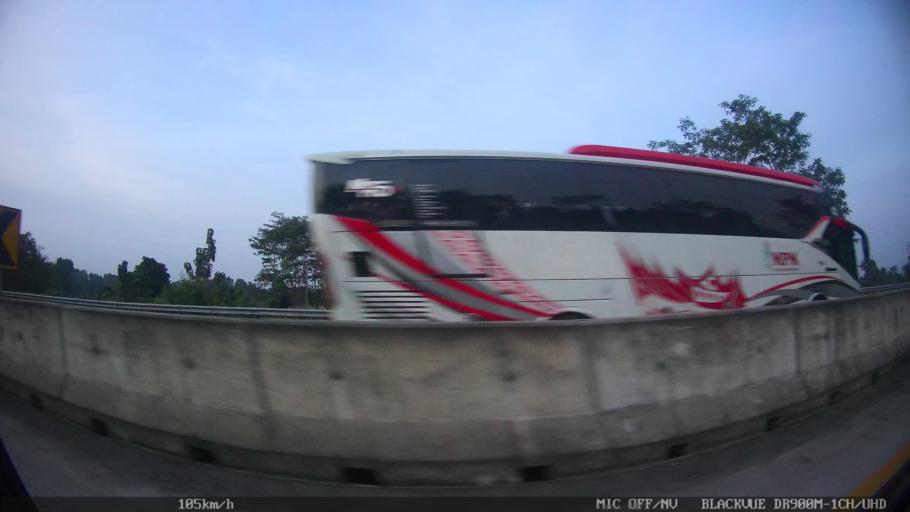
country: ID
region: Lampung
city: Penengahan
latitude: -5.7478
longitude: 105.7036
